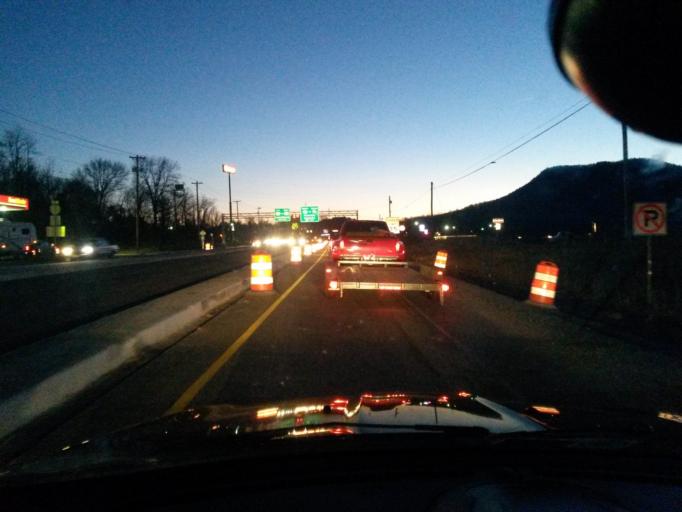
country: US
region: Virginia
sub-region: Botetourt County
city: Daleville
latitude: 37.3895
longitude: -79.9011
